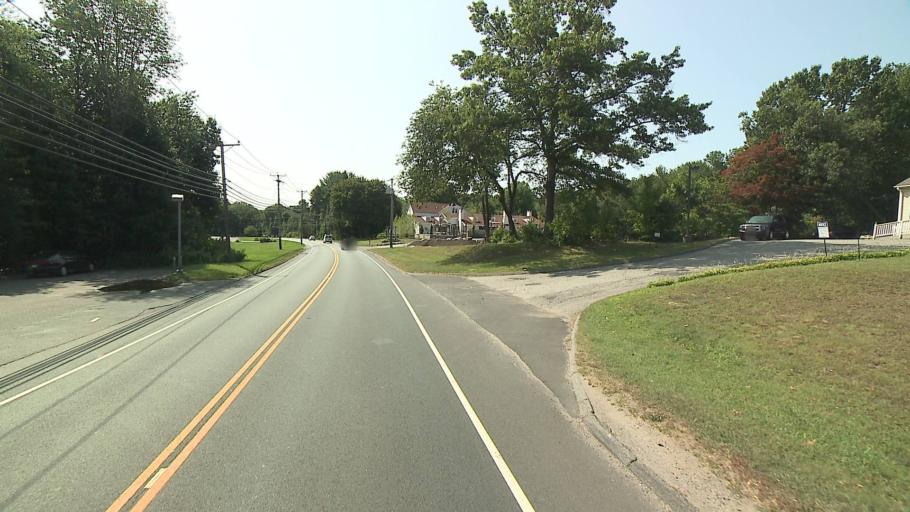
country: US
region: Connecticut
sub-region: Fairfield County
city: Newtown
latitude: 41.3838
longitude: -73.2849
